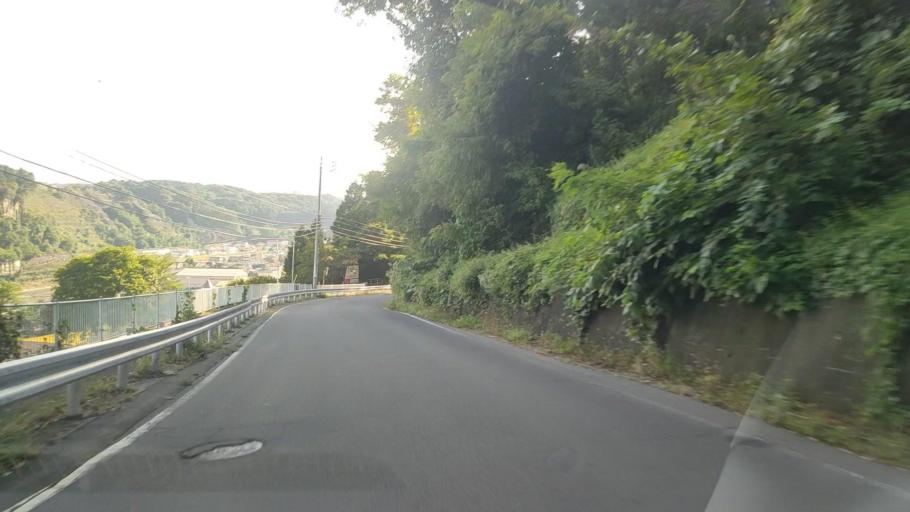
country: JP
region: Nagano
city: Komoro
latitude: 36.5406
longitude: 138.5535
